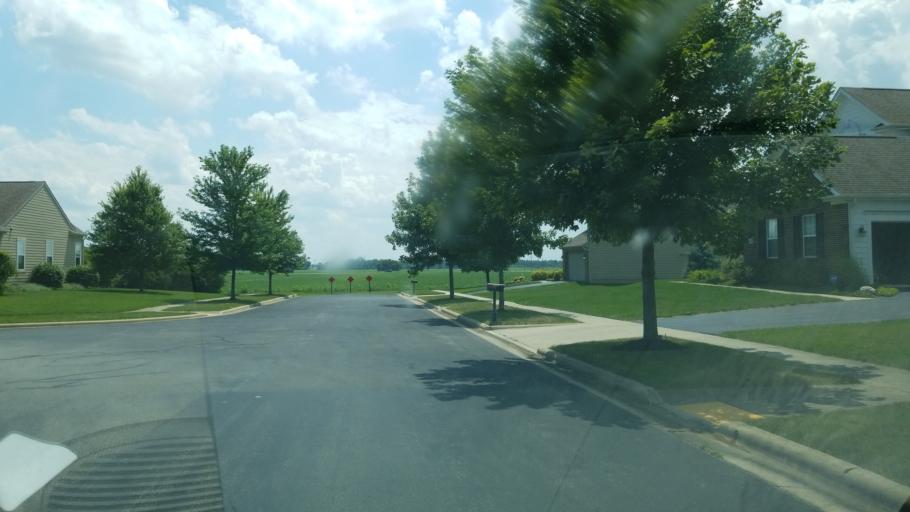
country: US
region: Ohio
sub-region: Delaware County
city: Lewis Center
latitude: 40.2214
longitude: -83.0060
